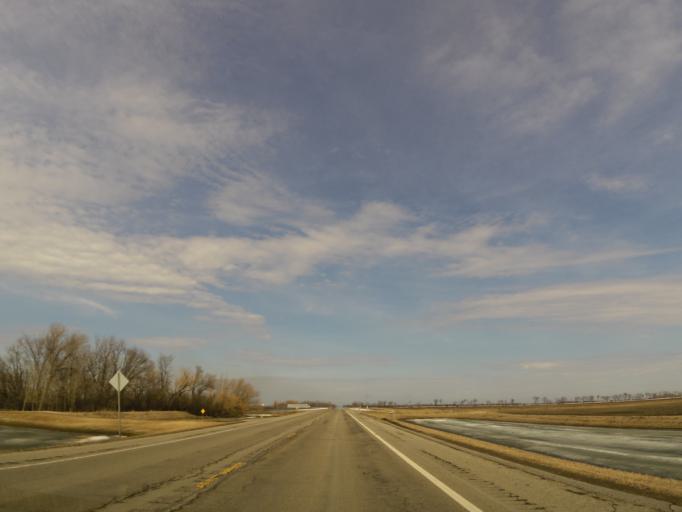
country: US
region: North Dakota
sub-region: Walsh County
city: Grafton
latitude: 48.3237
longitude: -97.4054
